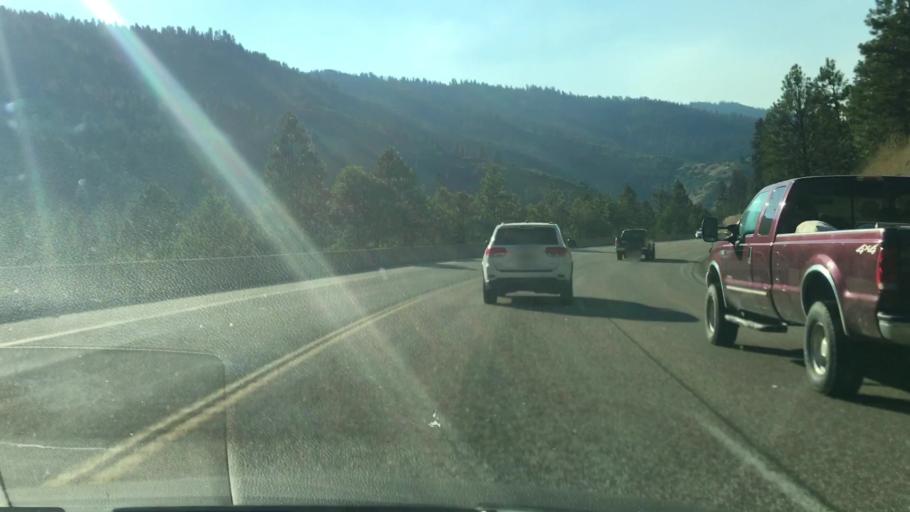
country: US
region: Idaho
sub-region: Boise County
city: Idaho City
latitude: 44.1090
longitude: -116.0980
